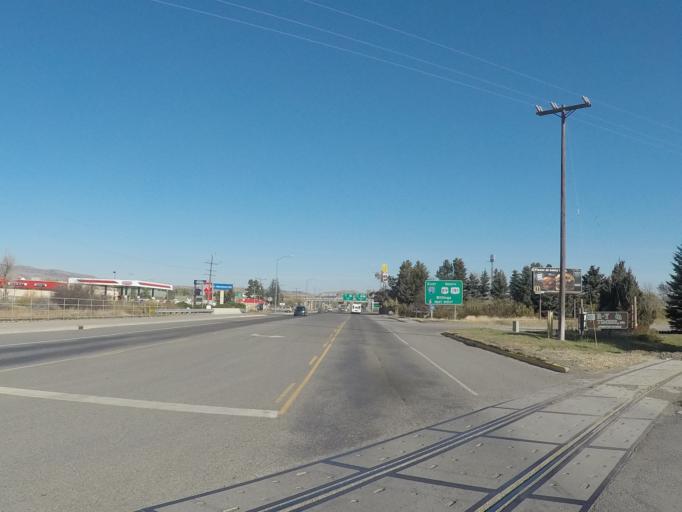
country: US
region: Montana
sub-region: Park County
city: Livingston
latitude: 45.6400
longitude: -110.5745
